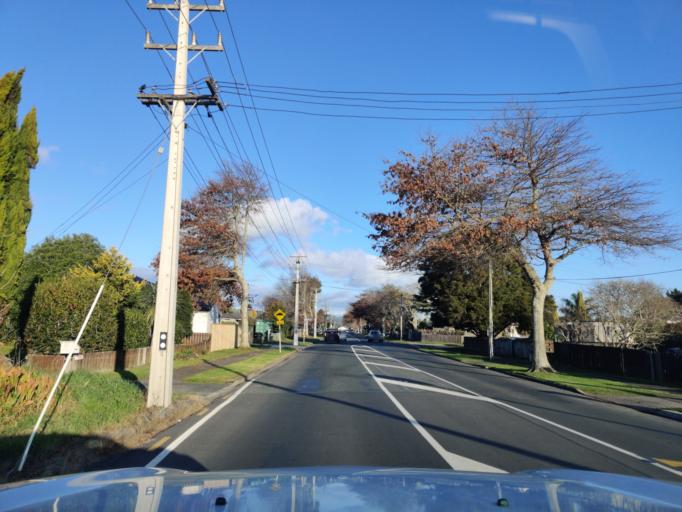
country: NZ
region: Auckland
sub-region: Auckland
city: Red Hill
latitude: -37.0507
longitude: 174.9563
